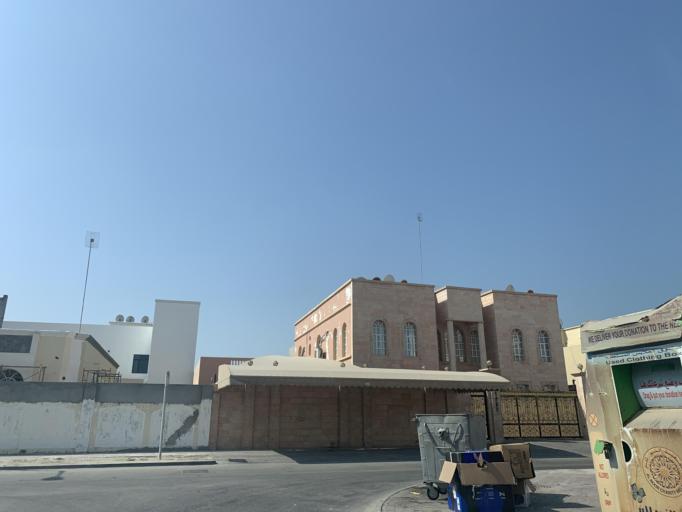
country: BH
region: Central Governorate
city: Madinat Hamad
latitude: 26.1344
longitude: 50.4940
